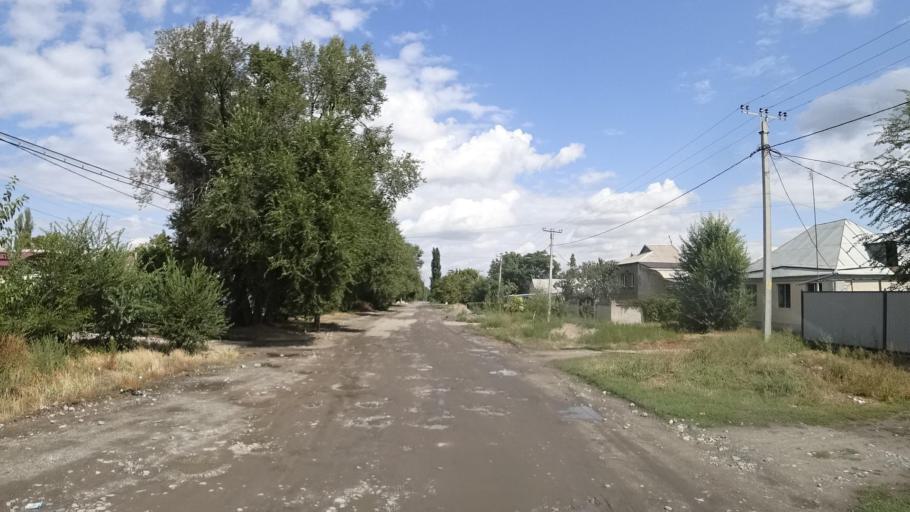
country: KG
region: Chuy
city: Lebedinovka
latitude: 42.8770
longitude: 74.7197
